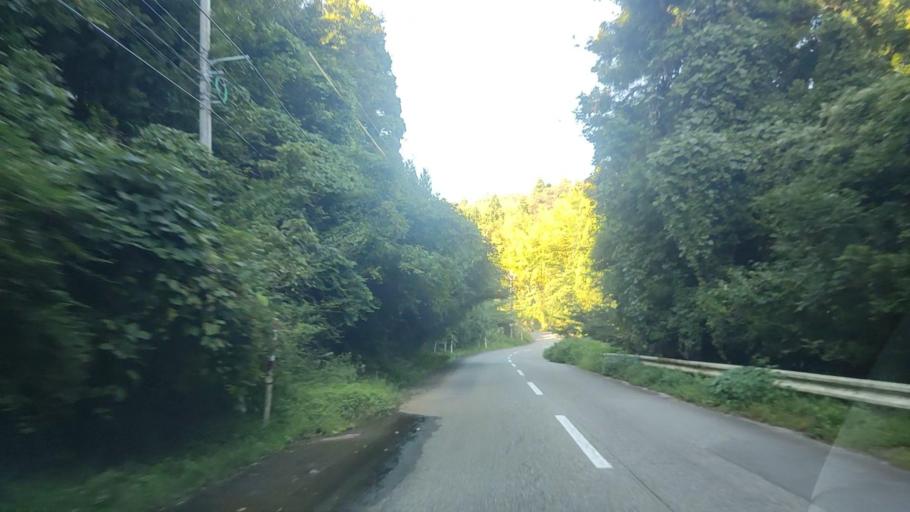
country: JP
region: Ishikawa
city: Nanao
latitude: 37.1140
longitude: 136.9651
